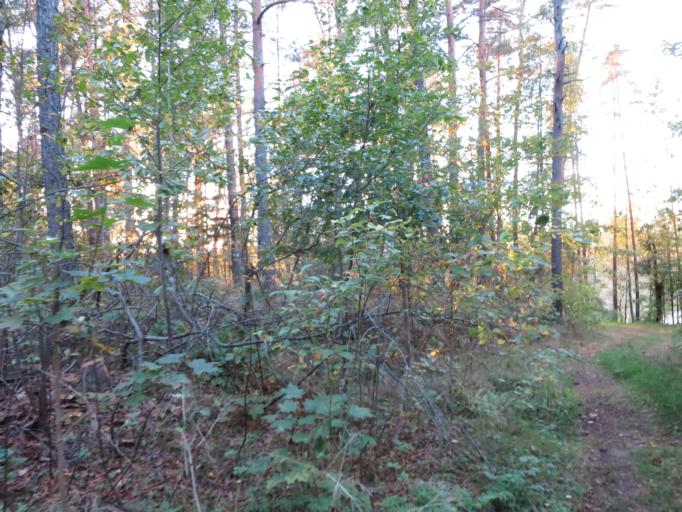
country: LV
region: Incukalns
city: Vangazi
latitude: 57.1266
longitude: 24.5608
